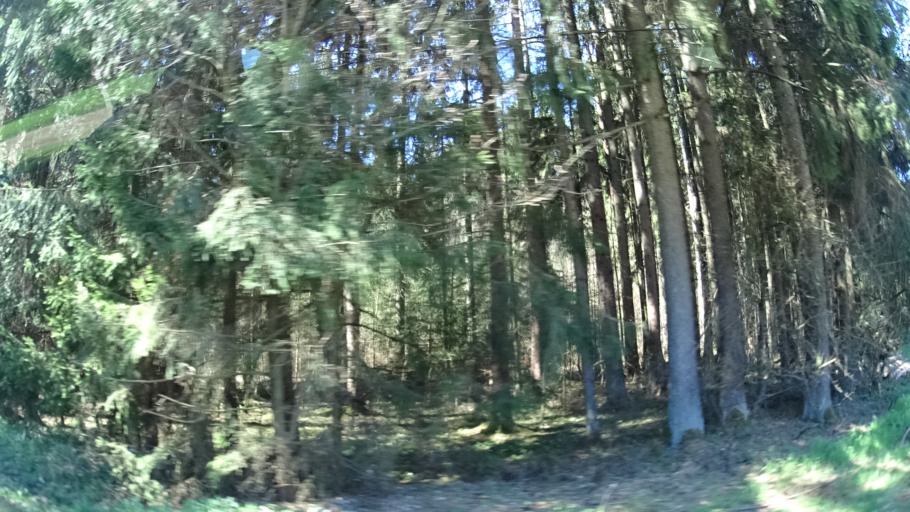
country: DE
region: Bavaria
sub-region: Upper Palatinate
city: Kastl
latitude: 49.3953
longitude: 11.6799
